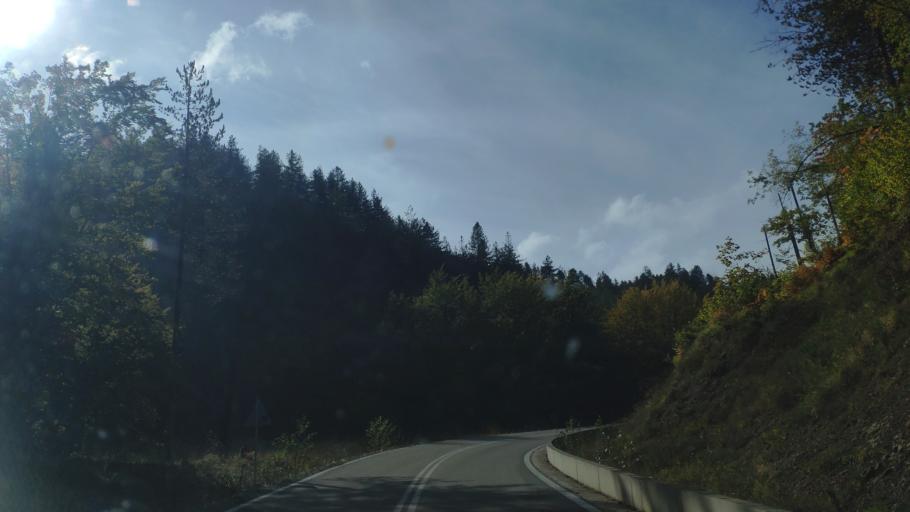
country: GR
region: West Macedonia
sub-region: Nomos Kastorias
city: Nestorio
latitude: 40.3775
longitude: 20.9414
